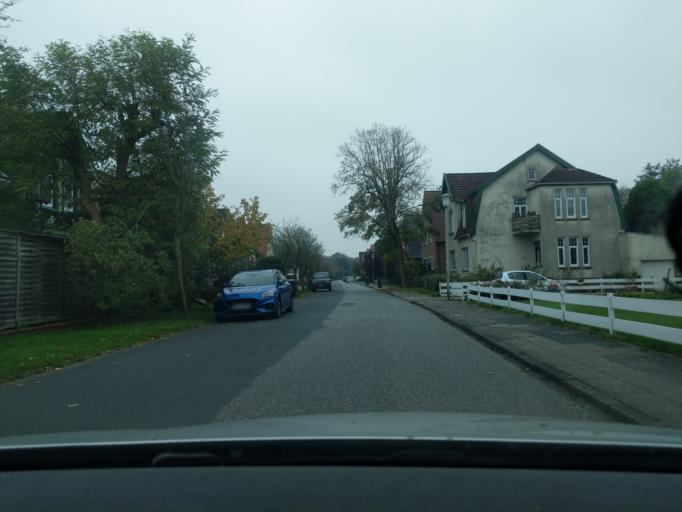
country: DE
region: Lower Saxony
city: Wanna
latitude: 53.8280
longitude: 8.7761
